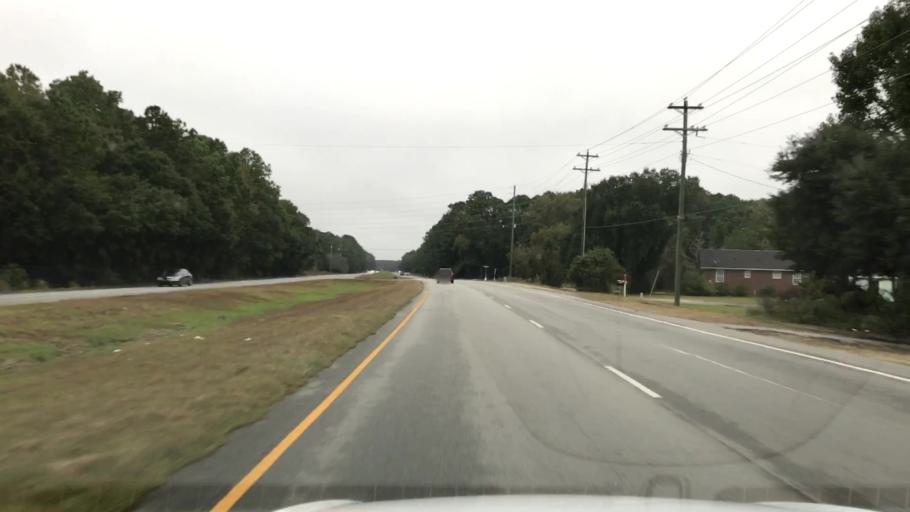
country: US
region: South Carolina
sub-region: Charleston County
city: Isle of Palms
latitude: 32.8890
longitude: -79.7419
